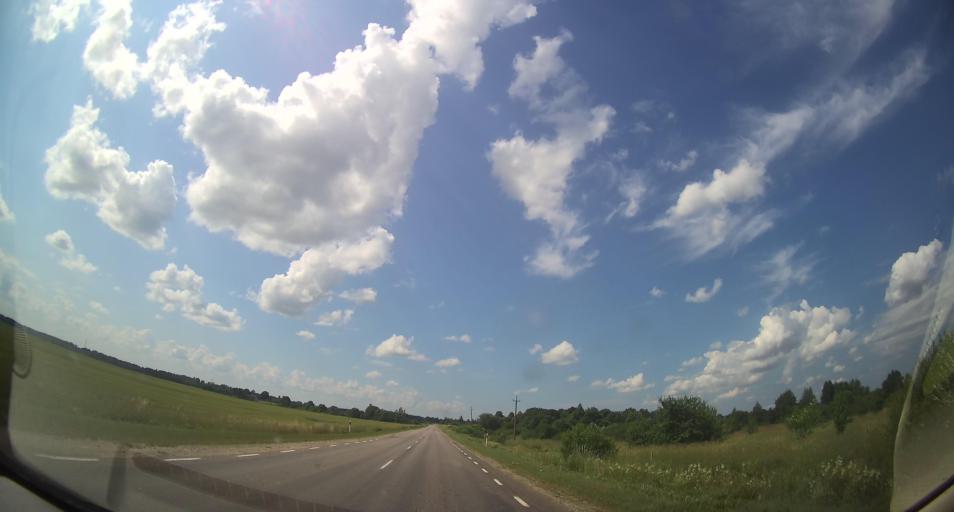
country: EE
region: Harju
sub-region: Nissi vald
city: Turba
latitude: 58.9164
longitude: 24.1580
